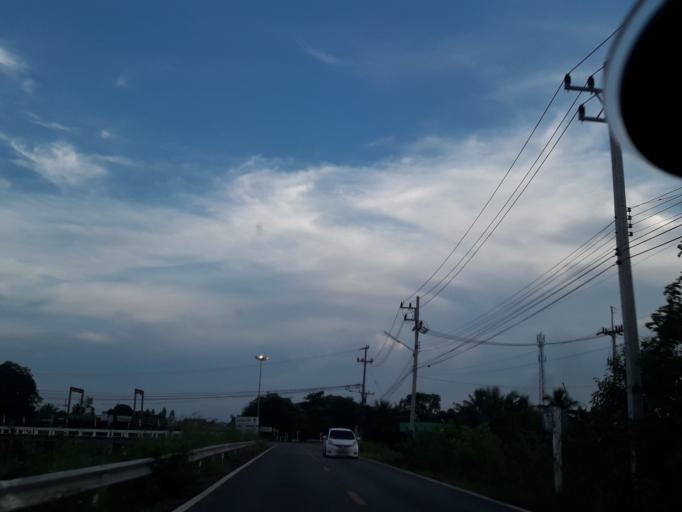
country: TH
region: Sara Buri
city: Nong Khae
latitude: 14.2777
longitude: 100.8912
